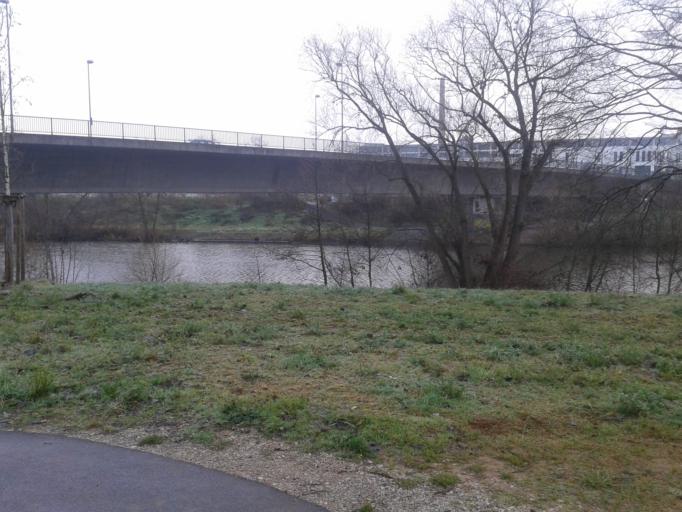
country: DE
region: Bavaria
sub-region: Upper Franconia
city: Bamberg
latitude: 49.9006
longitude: 10.8804
